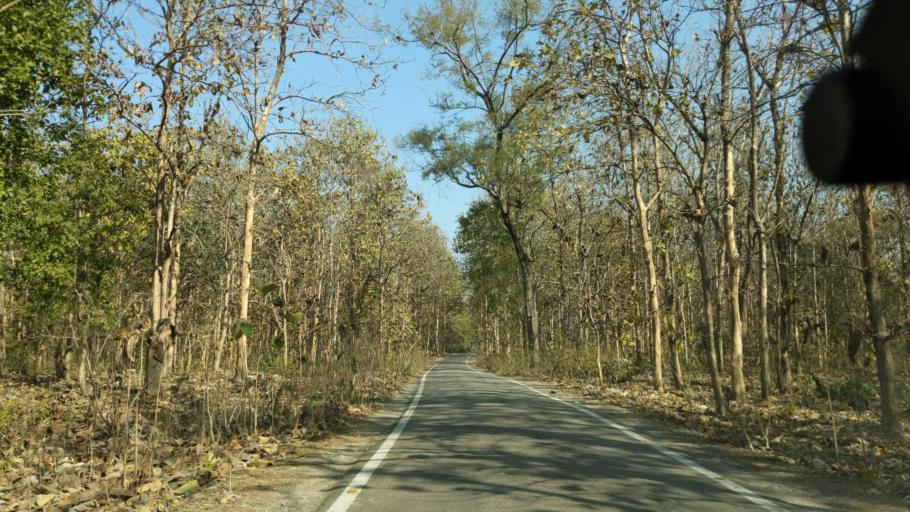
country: IN
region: Uttarakhand
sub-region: Naini Tal
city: Ramnagar
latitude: 29.4312
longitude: 79.1410
